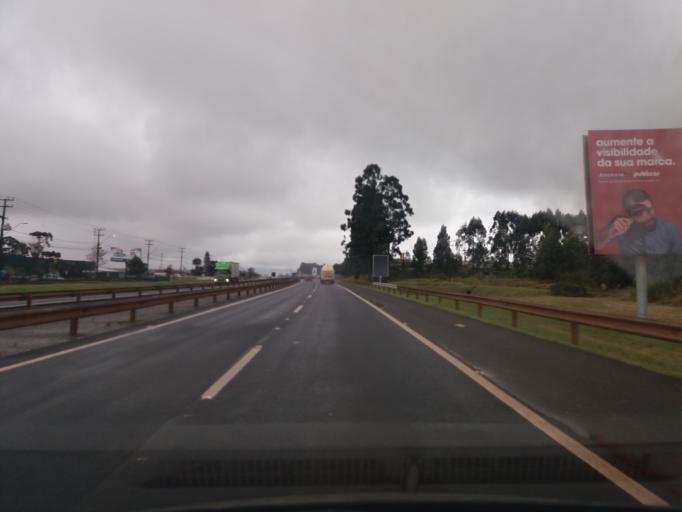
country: BR
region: Parana
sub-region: Cascavel
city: Cascavel
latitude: -24.9960
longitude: -53.5149
